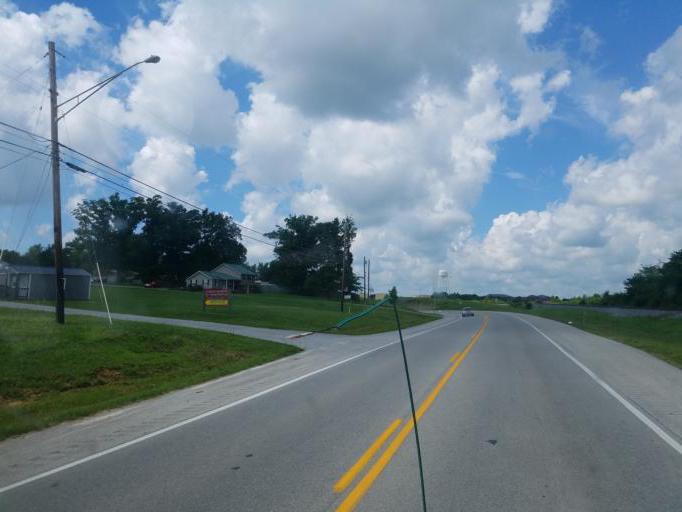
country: US
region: Kentucky
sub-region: Grayson County
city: Leitchfield
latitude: 37.4894
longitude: -86.2597
